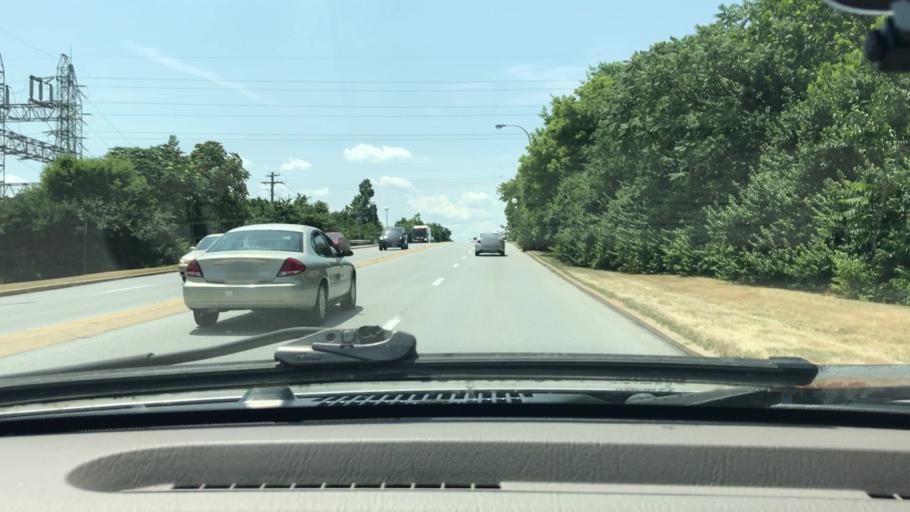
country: US
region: Pennsylvania
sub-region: Lancaster County
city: East Petersburg
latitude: 40.0713
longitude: -76.3356
